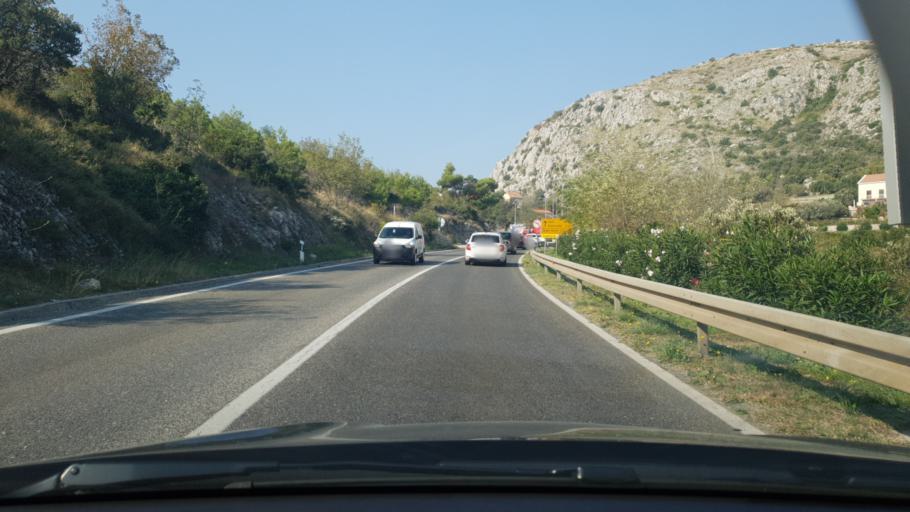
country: HR
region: Dubrovacko-Neretvanska
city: Cibaca
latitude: 42.6293
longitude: 18.1570
